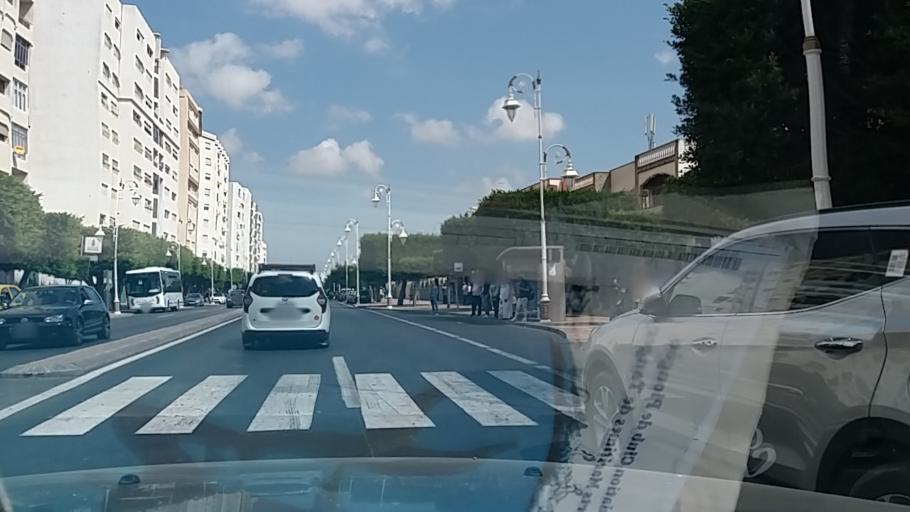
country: MA
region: Tanger-Tetouan
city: Tetouan
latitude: 35.5823
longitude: -5.3517
